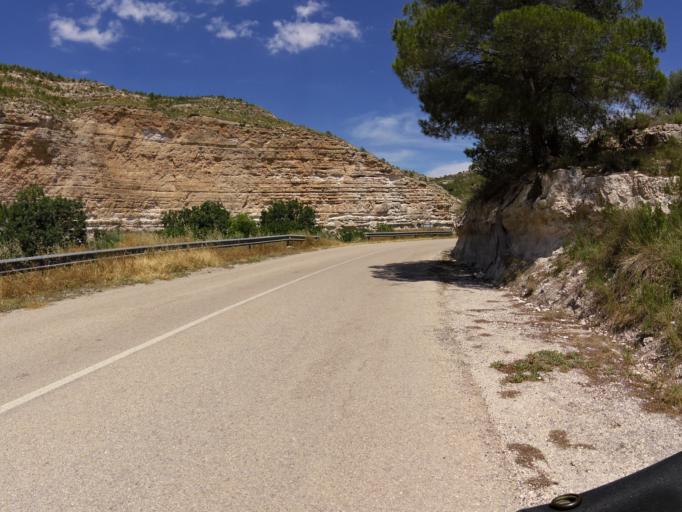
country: ES
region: Castille-La Mancha
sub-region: Provincia de Albacete
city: Jorquera
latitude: 39.1790
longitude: -1.5150
